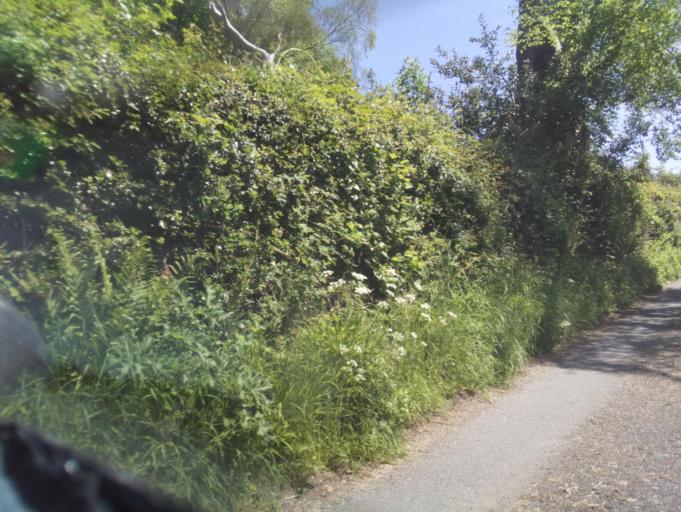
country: GB
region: Wales
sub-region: Monmouthshire
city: Tintern
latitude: 51.6643
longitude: -2.7495
